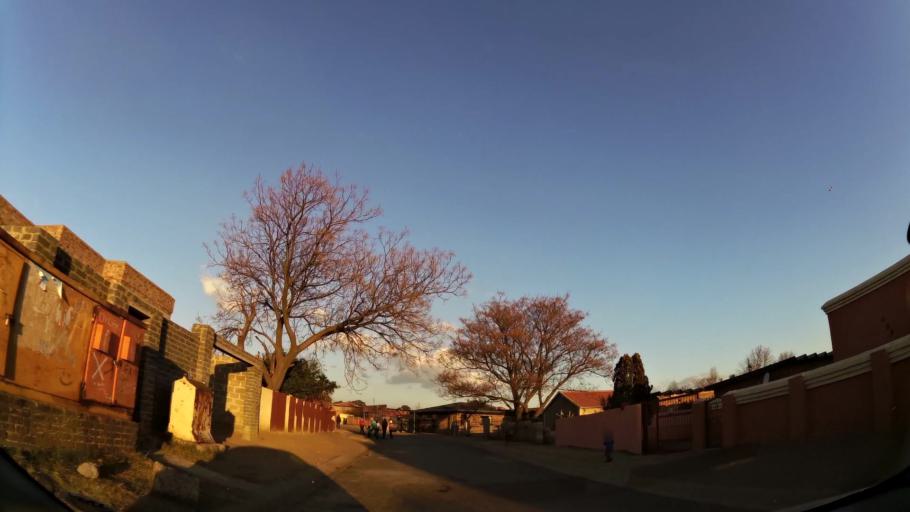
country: ZA
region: Mpumalanga
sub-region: Nkangala District Municipality
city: Witbank
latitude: -25.8861
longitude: 29.1828
